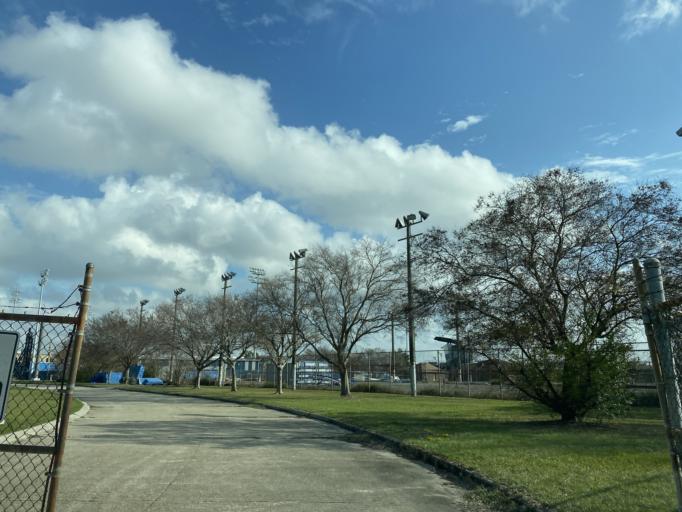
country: US
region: Louisiana
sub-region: Orleans Parish
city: New Orleans
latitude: 30.0312
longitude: -90.0491
